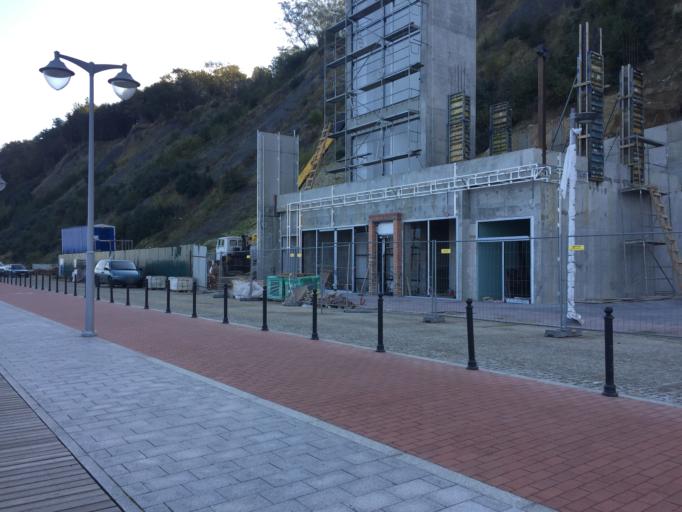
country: RU
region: Kaliningrad
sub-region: Gorod Svetlogorsk
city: Svetlogorsk
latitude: 54.9470
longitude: 20.1599
